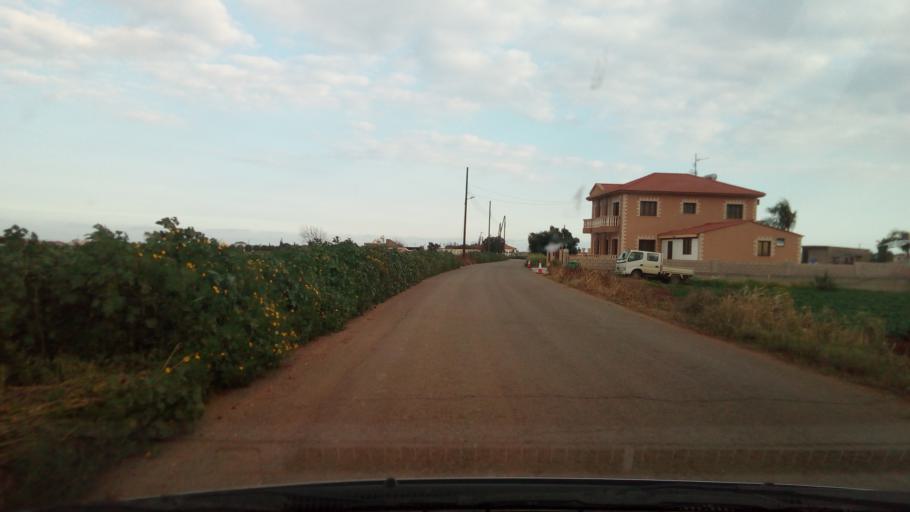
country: CY
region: Ammochostos
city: Avgorou
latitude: 34.9843
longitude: 33.8376
